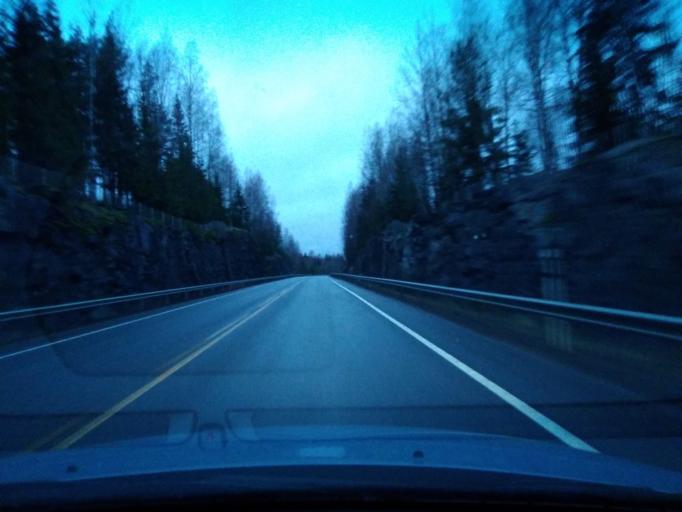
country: FI
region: Uusimaa
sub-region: Porvoo
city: Porvoo
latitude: 60.4056
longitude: 25.5885
